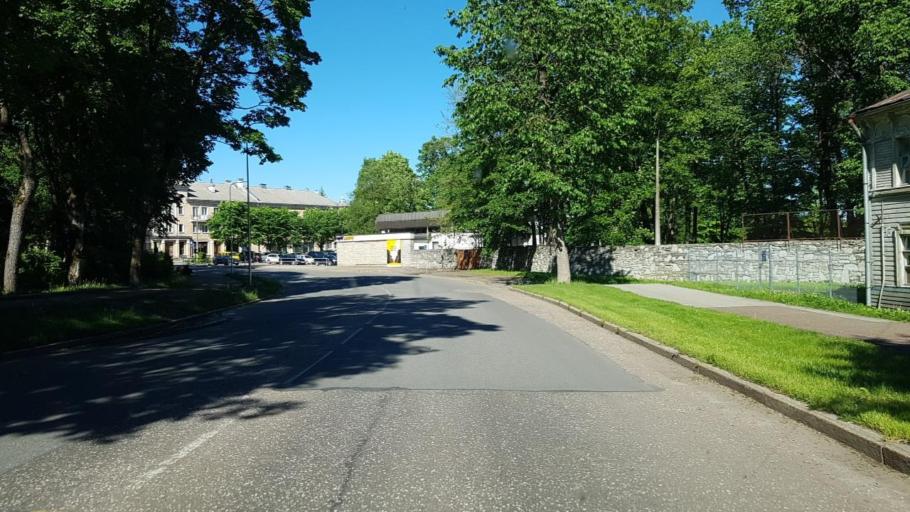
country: EE
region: Ida-Virumaa
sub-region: Narva linn
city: Narva
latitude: 59.3605
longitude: 28.1940
